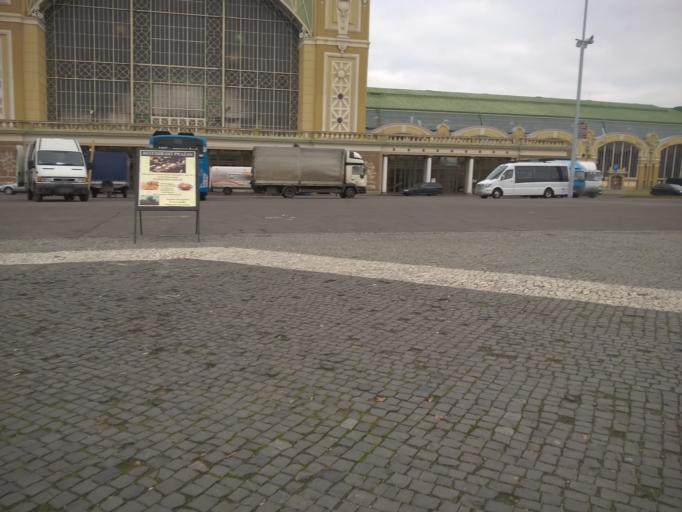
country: CZ
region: Praha
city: Prague
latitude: 50.1058
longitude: 14.4304
